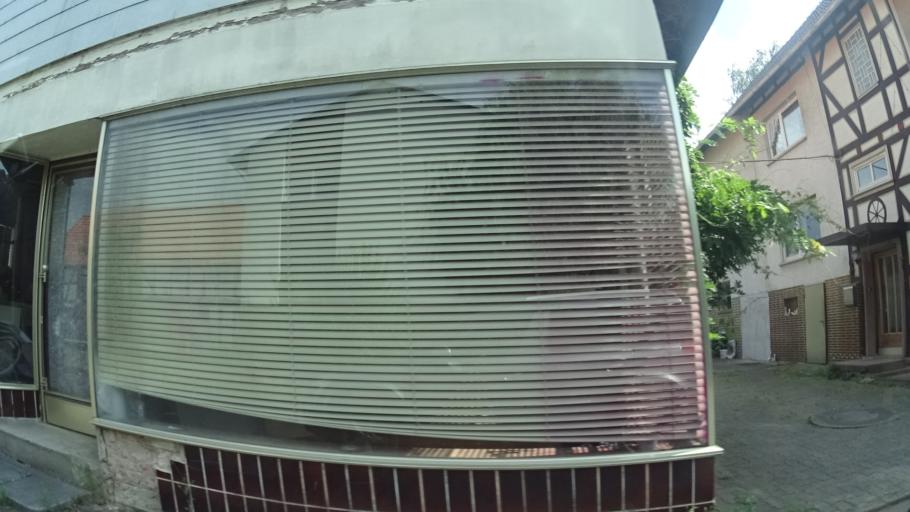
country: DE
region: Hesse
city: Grebenau
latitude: 50.7413
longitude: 9.4718
